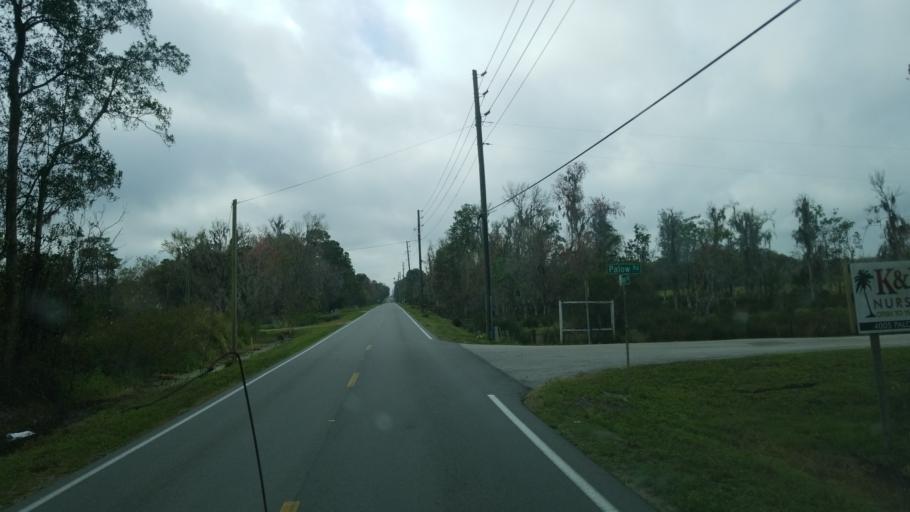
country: US
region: Florida
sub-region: Polk County
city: Kathleen
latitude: 28.1539
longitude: -82.0234
